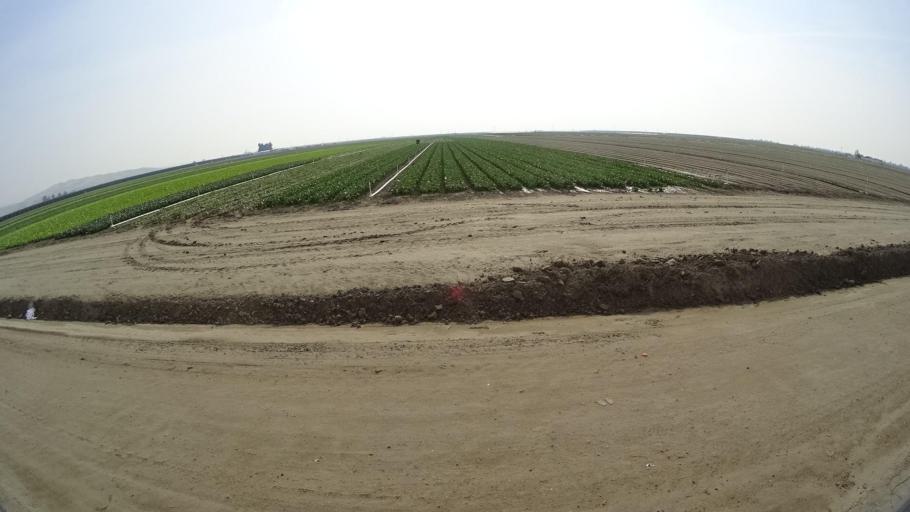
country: US
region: California
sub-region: Kern County
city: Arvin
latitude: 35.1508
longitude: -118.8638
